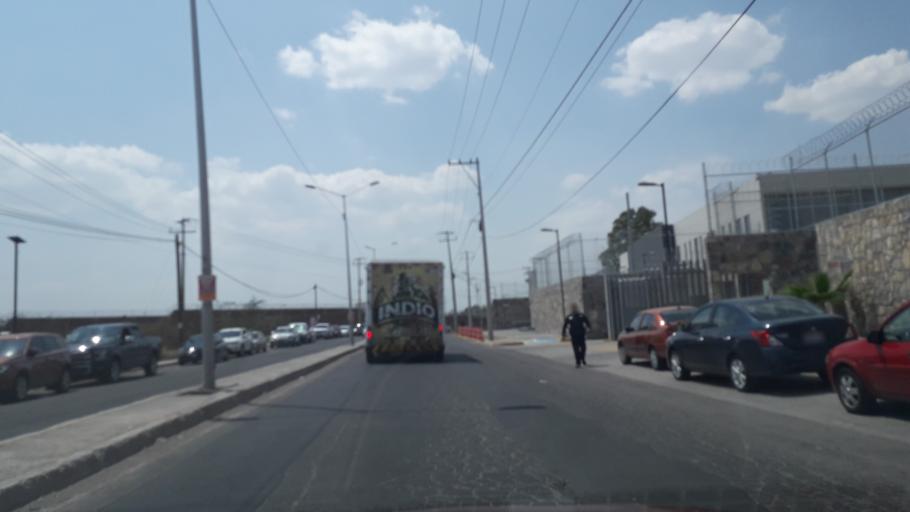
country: MX
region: Puebla
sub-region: Puebla
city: Galaxia la Calera
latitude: 18.9915
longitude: -98.1704
